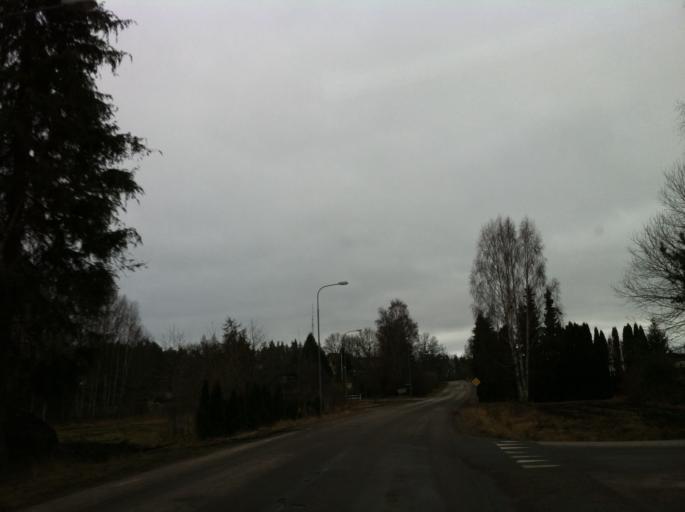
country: SE
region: Kalmar
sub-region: Vasterviks Kommun
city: Vaestervik
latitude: 57.8064
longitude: 16.5944
